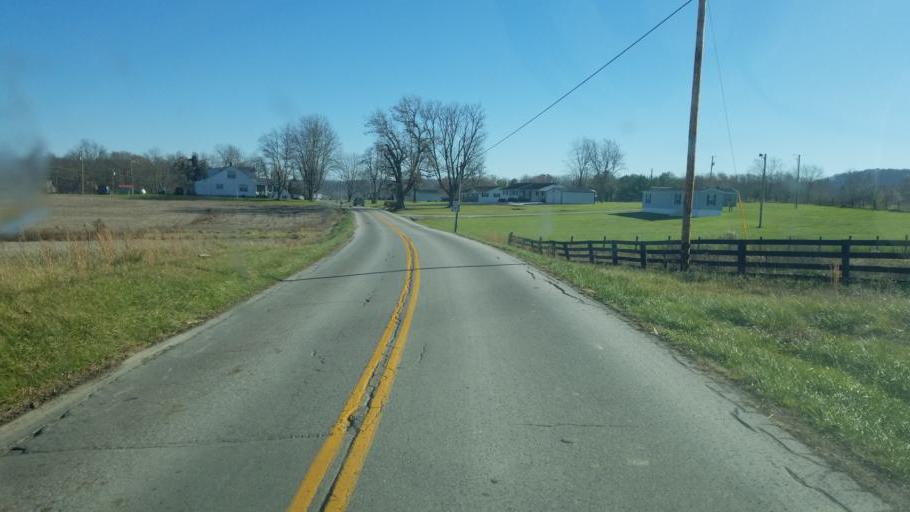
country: US
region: Kentucky
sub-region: Fleming County
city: Flemingsburg
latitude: 38.4792
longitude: -83.6063
